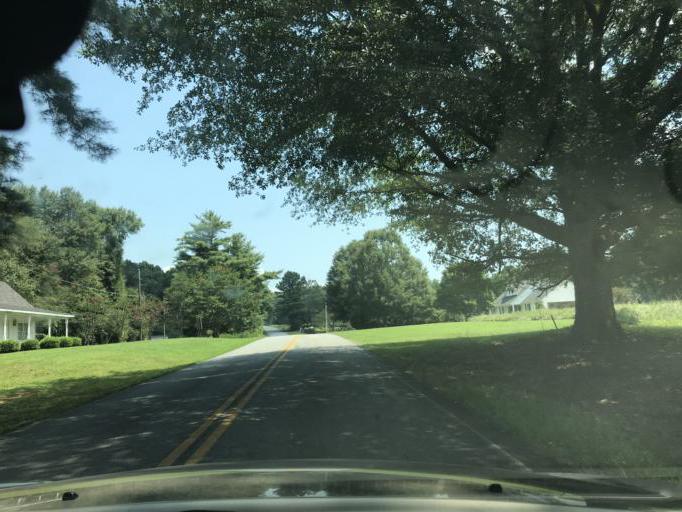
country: US
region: Georgia
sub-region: Dawson County
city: Dawsonville
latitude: 34.3257
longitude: -84.0896
